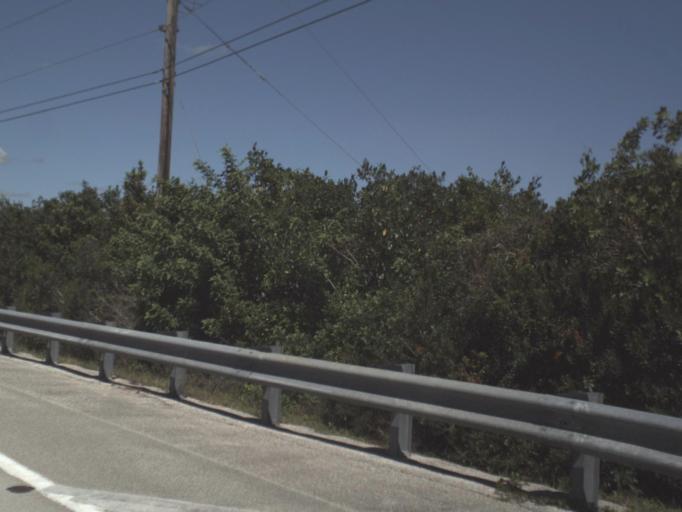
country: US
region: Florida
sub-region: Collier County
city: Lely Resort
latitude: 25.9860
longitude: -81.5684
